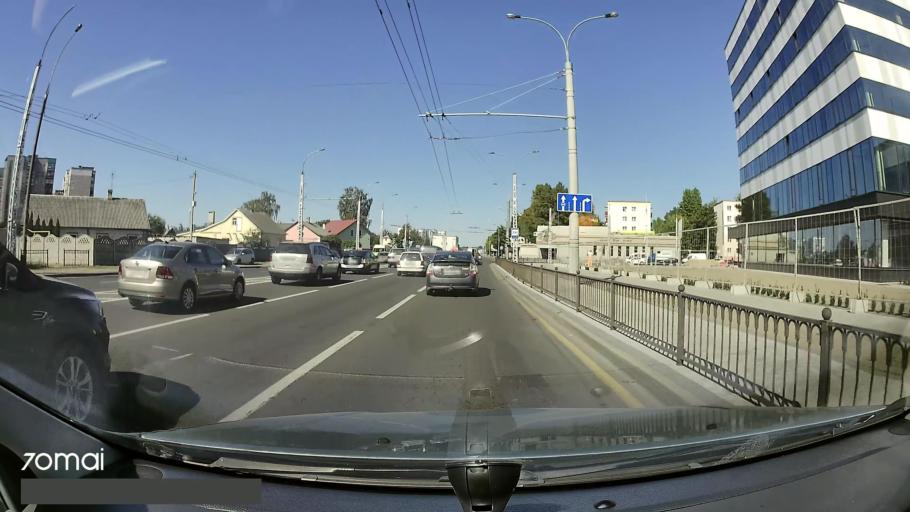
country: BY
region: Brest
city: Brest
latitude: 52.0986
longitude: 23.7281
